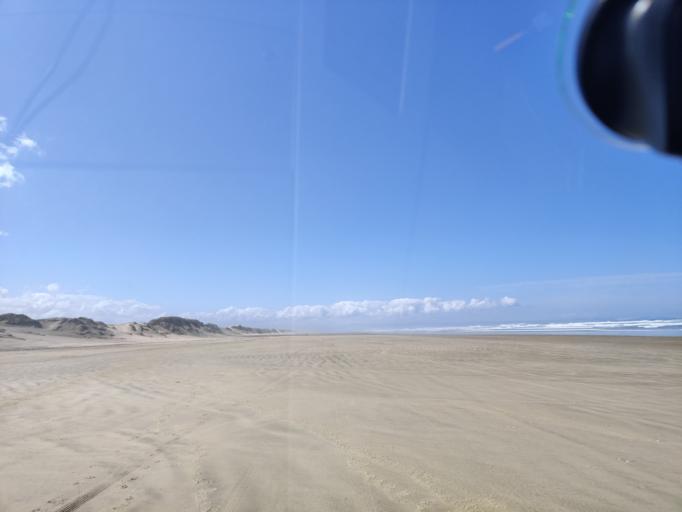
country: NZ
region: Northland
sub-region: Far North District
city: Ahipara
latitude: -34.9033
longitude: 173.0874
